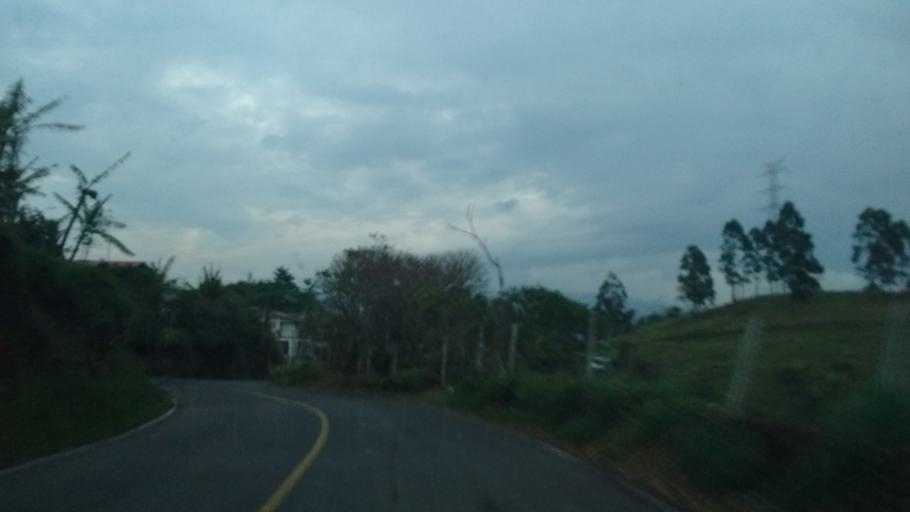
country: CO
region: Cauca
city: Popayan
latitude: 2.3760
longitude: -76.6993
